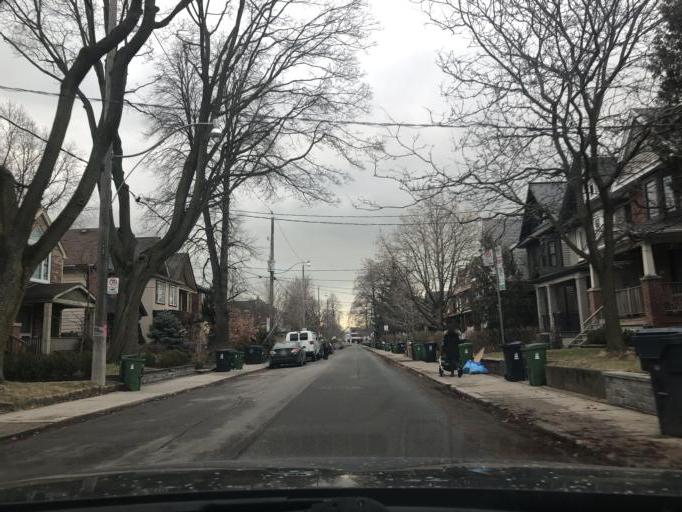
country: CA
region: Ontario
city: Toronto
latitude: 43.6810
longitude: -79.3519
